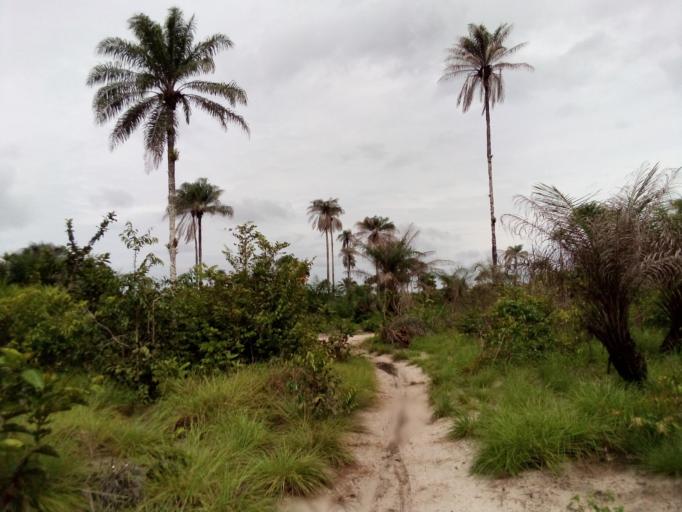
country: SL
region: Southern Province
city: Bonthe
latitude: 7.5201
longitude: -12.5733
